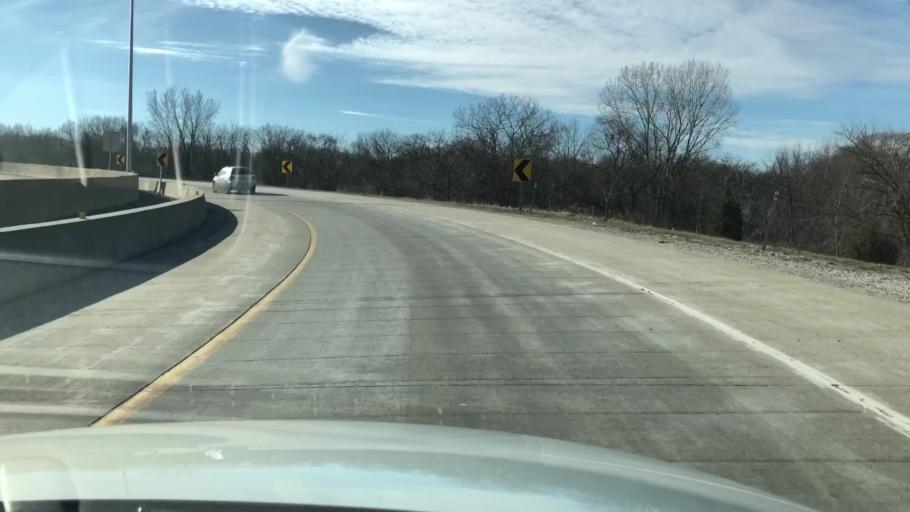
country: US
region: Wisconsin
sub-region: Milwaukee County
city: Greendale
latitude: 42.9417
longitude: -87.9376
